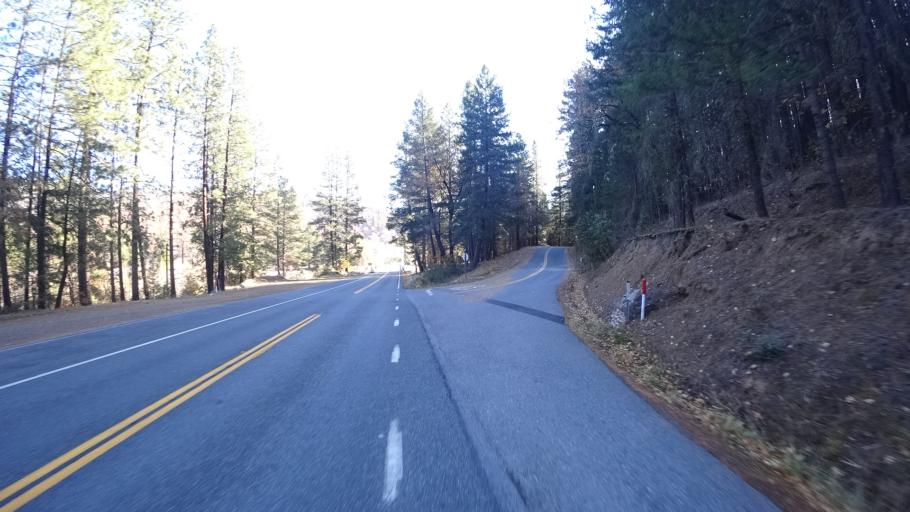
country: US
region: California
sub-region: Siskiyou County
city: Yreka
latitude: 41.8267
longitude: -122.9798
